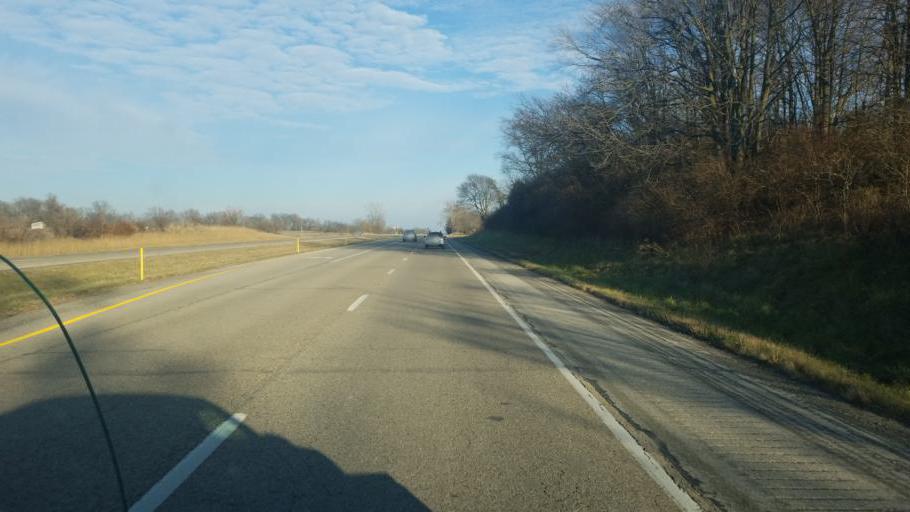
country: US
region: Indiana
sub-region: Knox County
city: Vincennes
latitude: 38.6767
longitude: -87.4226
